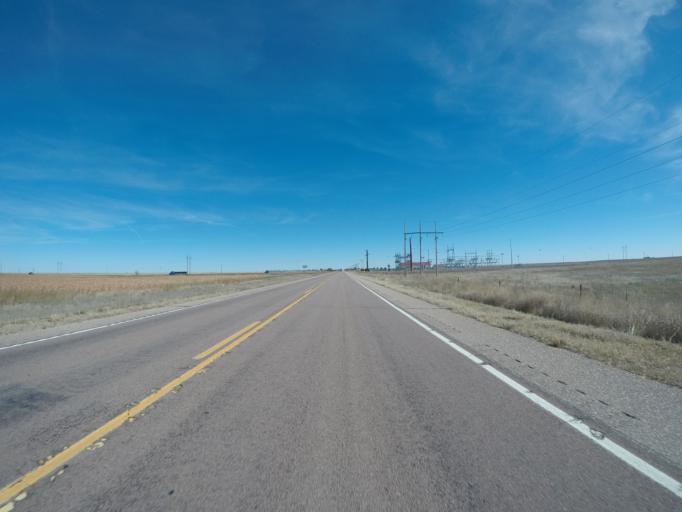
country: US
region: Colorado
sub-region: Yuma County
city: Yuma
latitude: 39.6559
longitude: -102.7100
